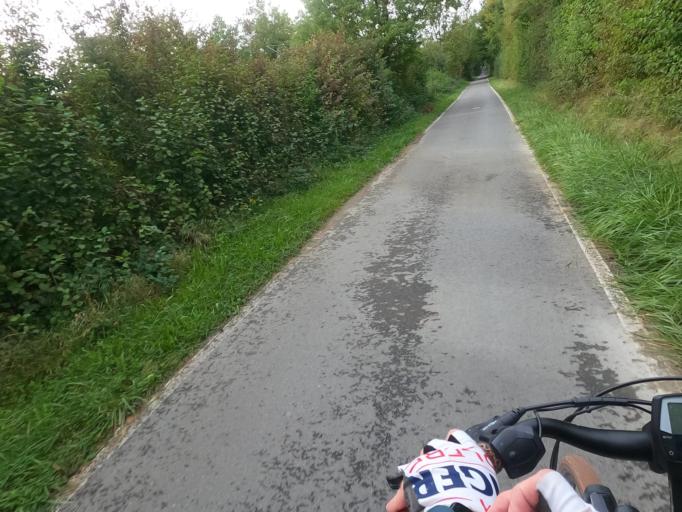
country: CH
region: Thurgau
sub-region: Kreuzlingen District
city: Ermatingen
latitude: 47.6981
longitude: 9.1108
